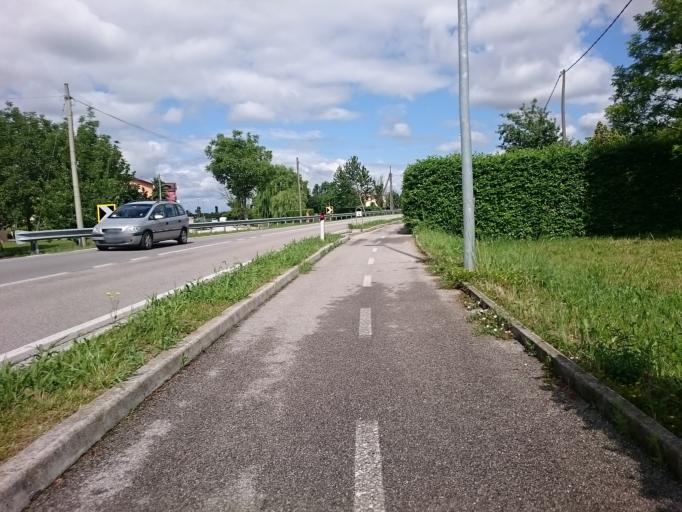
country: IT
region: Veneto
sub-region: Provincia di Padova
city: Mestrino
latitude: 45.4473
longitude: 11.7572
